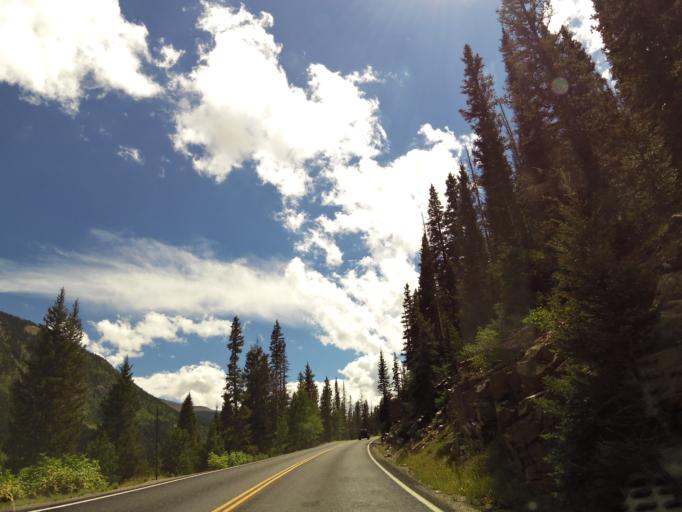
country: US
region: Colorado
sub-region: San Juan County
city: Silverton
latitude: 37.7991
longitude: -107.6746
